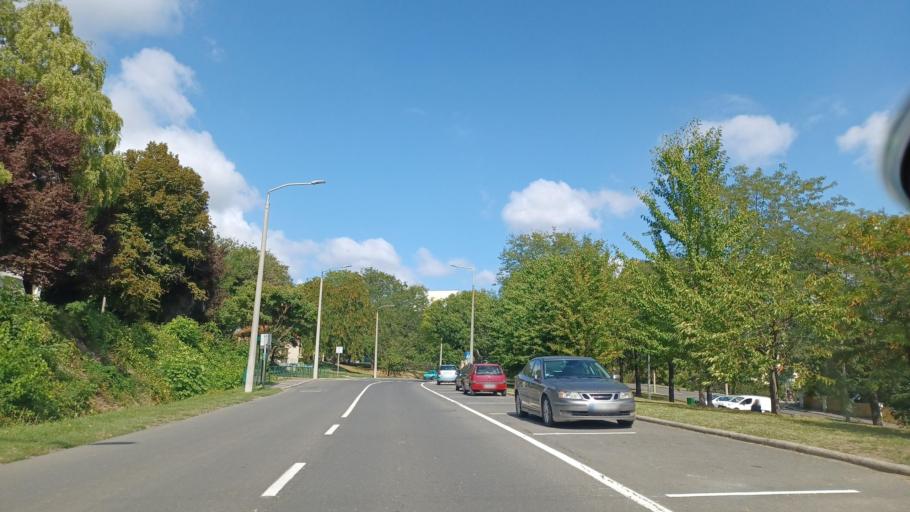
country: HU
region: Tolna
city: Szekszard
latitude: 46.3350
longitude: 18.6968
